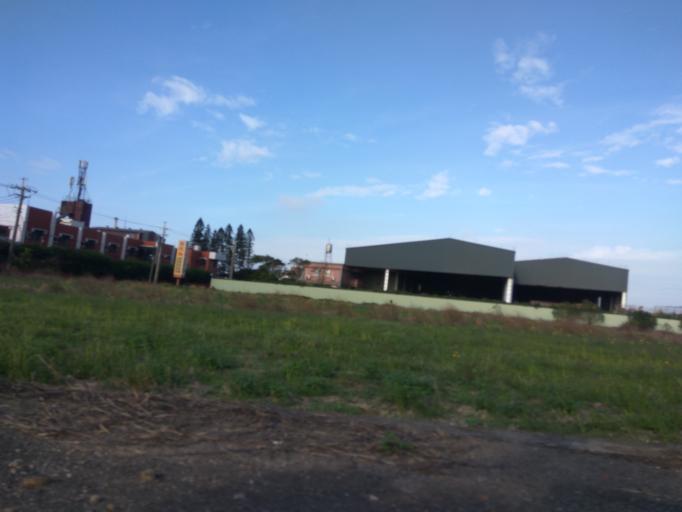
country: TW
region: Taiwan
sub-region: Hsinchu
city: Zhubei
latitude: 24.9832
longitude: 121.0379
